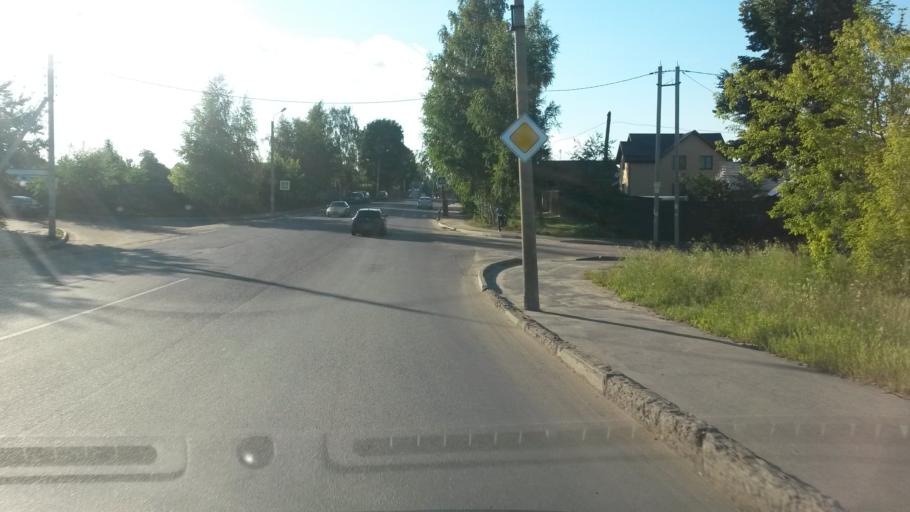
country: RU
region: Ivanovo
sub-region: Gorod Ivanovo
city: Ivanovo
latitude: 57.0178
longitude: 40.9246
